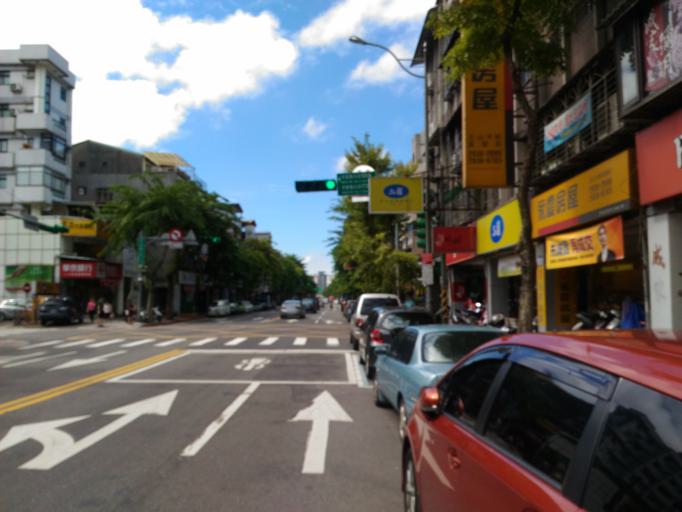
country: TW
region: Taipei
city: Taipei
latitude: 24.9820
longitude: 121.5614
